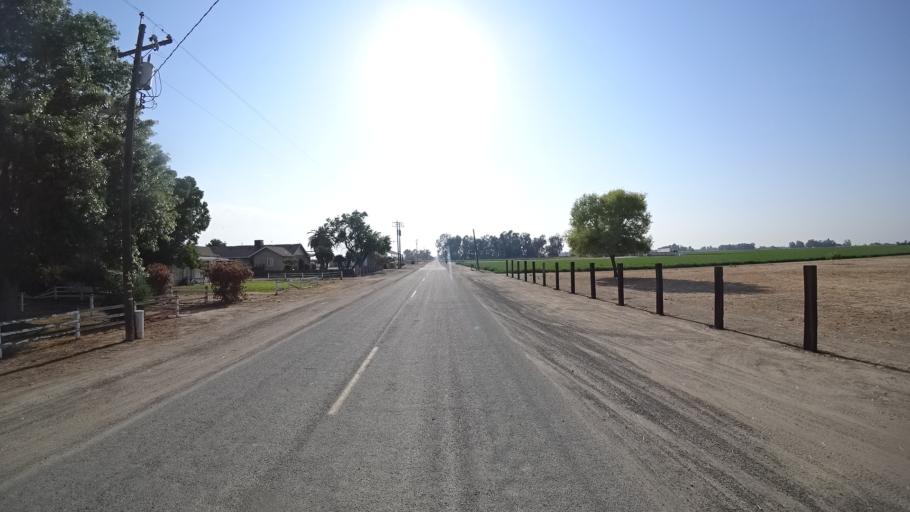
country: US
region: California
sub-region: Fresno County
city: Riverdale
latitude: 36.3585
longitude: -119.8803
